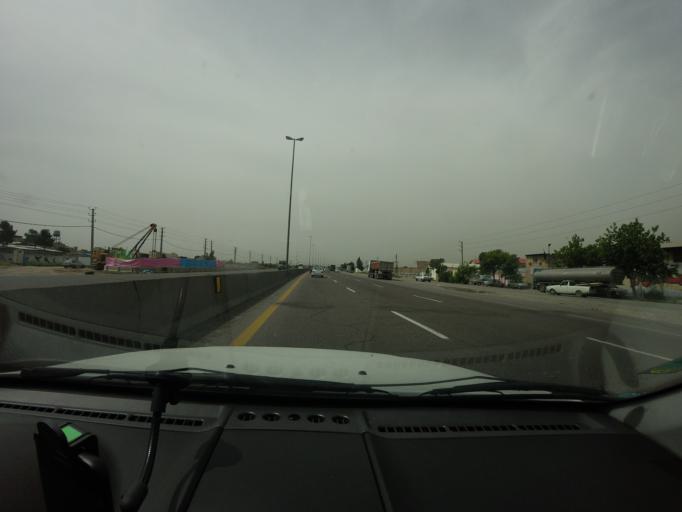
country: IR
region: Tehran
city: Robat Karim
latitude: 35.5504
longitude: 51.1245
